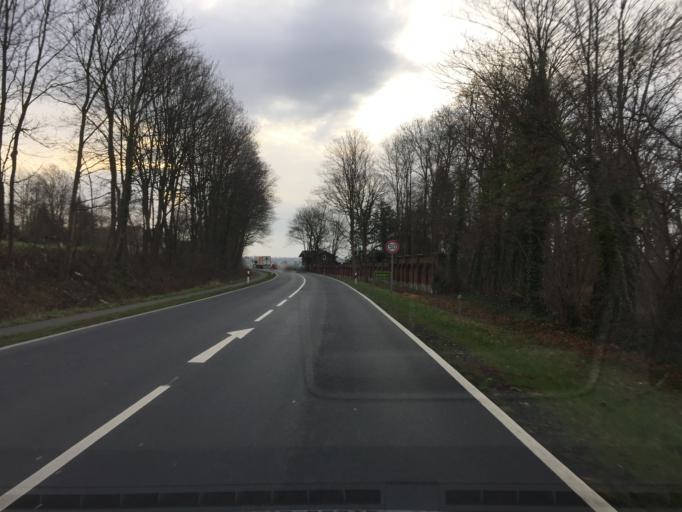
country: DE
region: Lower Saxony
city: Gehrden
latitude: 52.3312
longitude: 9.6097
